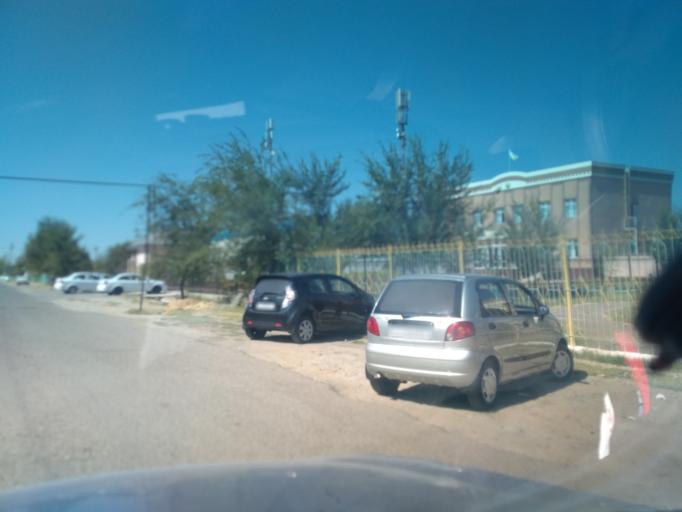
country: UZ
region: Sirdaryo
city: Guliston
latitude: 40.4958
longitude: 68.7044
